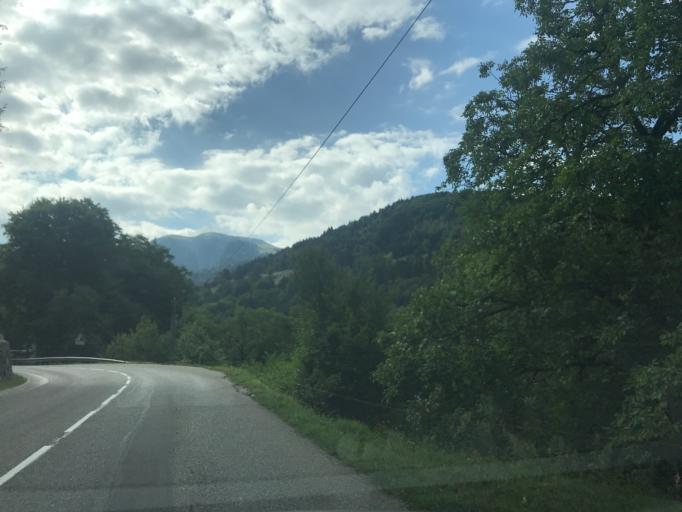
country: FR
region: Rhone-Alpes
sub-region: Departement de la Haute-Savoie
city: Thones
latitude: 45.8600
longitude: 6.3358
